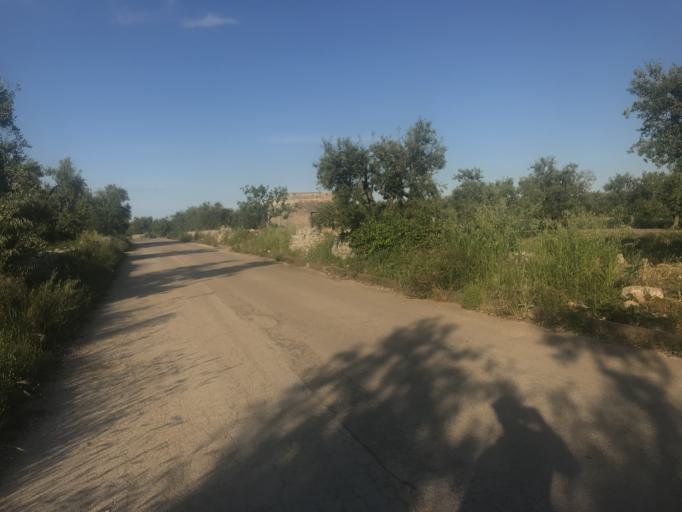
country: IT
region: Apulia
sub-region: Provincia di Bari
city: Corato
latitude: 41.1606
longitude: 16.4188
